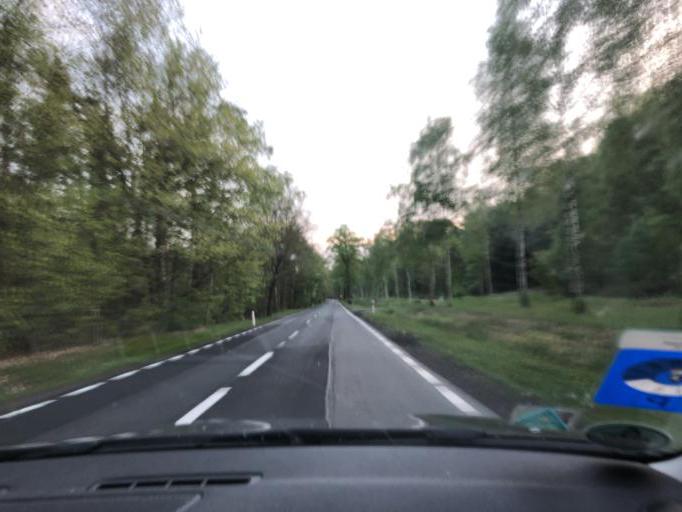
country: PL
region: Lubusz
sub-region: Powiat zarski
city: Trzebiel
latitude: 51.6210
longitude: 14.7965
